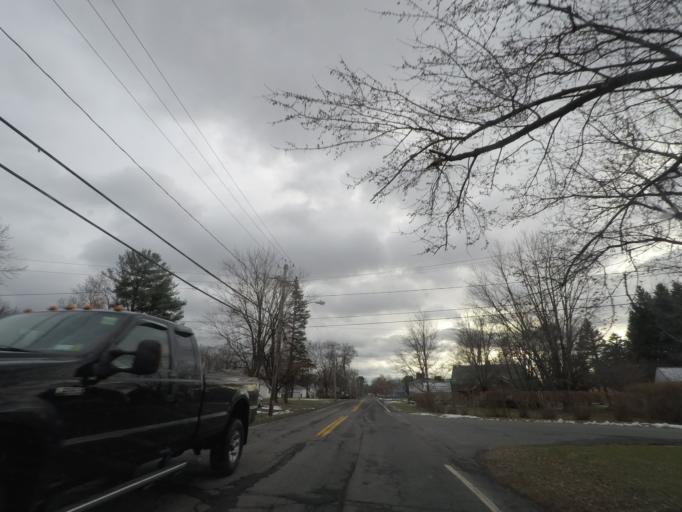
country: US
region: New York
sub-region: Rensselaer County
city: East Greenbush
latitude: 42.6029
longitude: -73.7184
